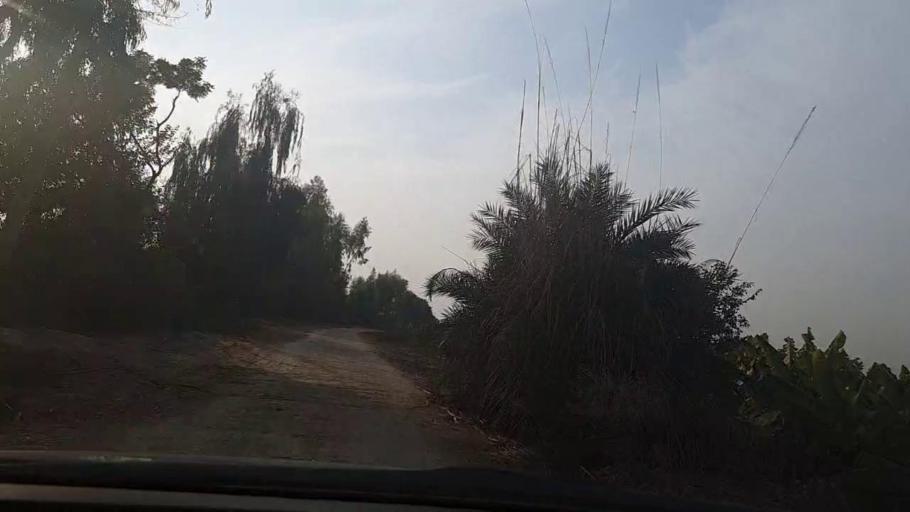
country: PK
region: Sindh
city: Daulatpur
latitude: 26.3323
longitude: 68.0455
